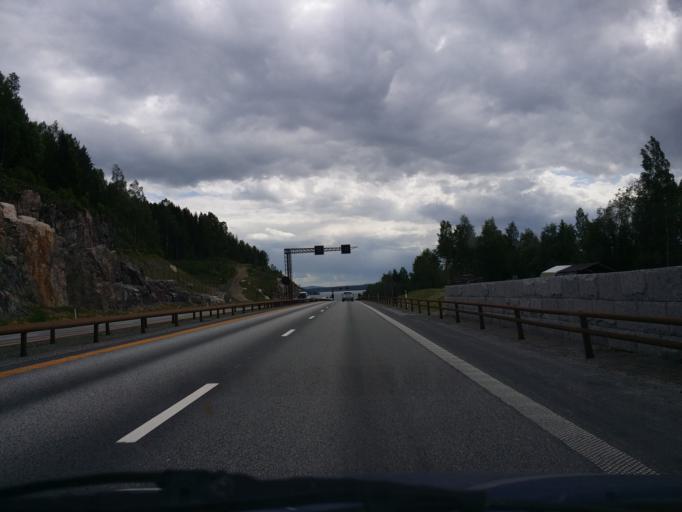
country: NO
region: Akershus
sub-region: Eidsvoll
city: Eidsvoll
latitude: 60.4928
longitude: 11.2364
